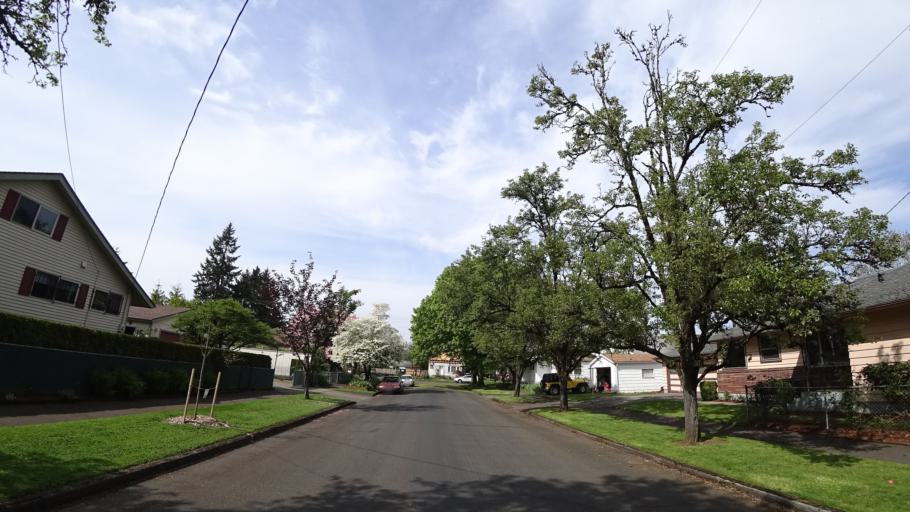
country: US
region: Oregon
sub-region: Multnomah County
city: Lents
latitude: 45.4801
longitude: -122.6100
